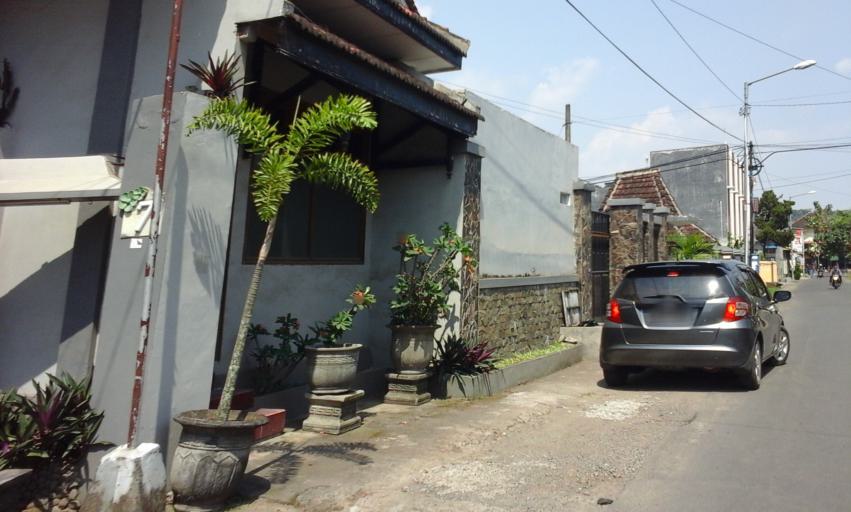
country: ID
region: East Java
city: Sumbersari Wetan
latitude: -8.1713
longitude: 113.7113
